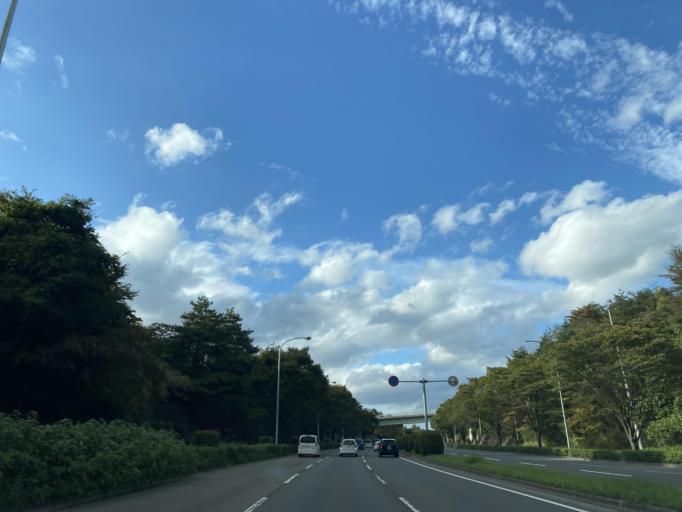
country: JP
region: Miyagi
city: Sendai-shi
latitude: 38.3119
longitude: 140.8464
